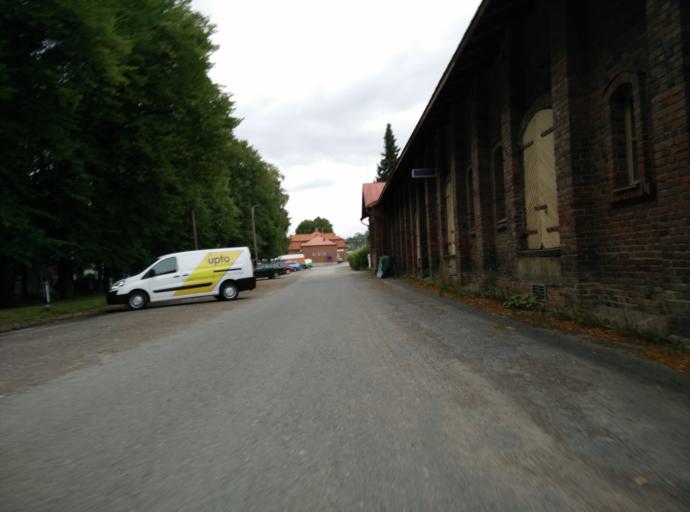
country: FI
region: Haeme
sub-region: Haemeenlinna
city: Haemeenlinna
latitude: 61.0011
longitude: 24.4808
